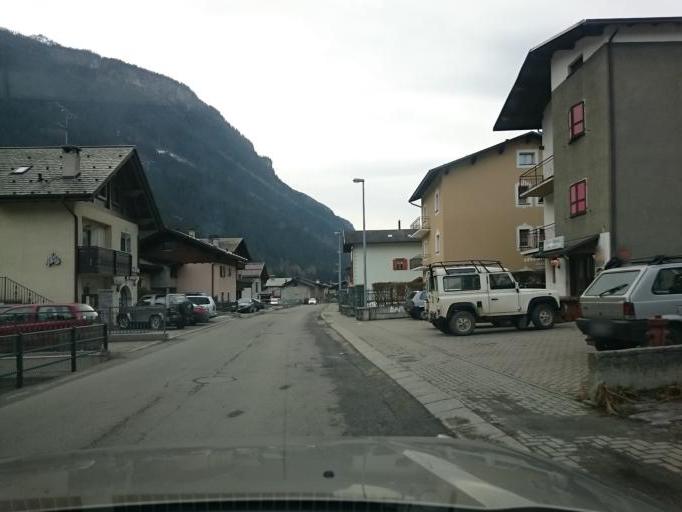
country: IT
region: Lombardy
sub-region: Provincia di Sondrio
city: Cepina
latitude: 46.4360
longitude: 10.3576
